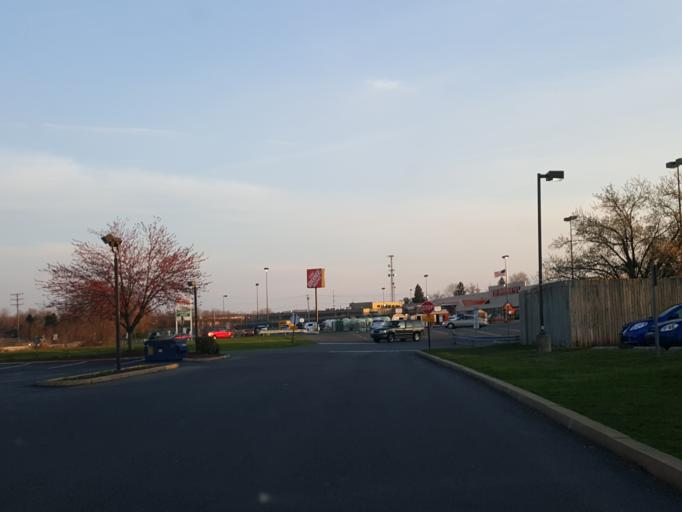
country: US
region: Pennsylvania
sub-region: Lebanon County
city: Hebron
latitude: 40.3423
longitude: -76.3978
